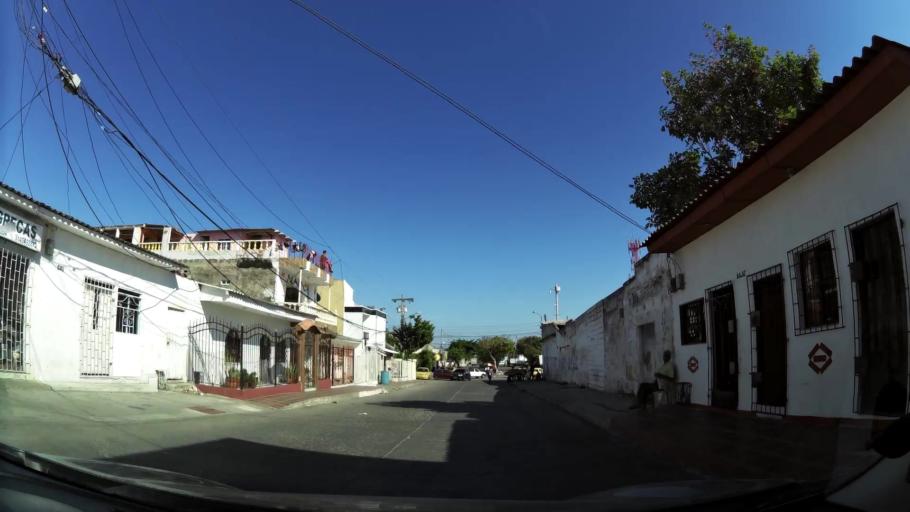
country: CO
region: Atlantico
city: Barranquilla
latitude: 10.9655
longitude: -74.7912
